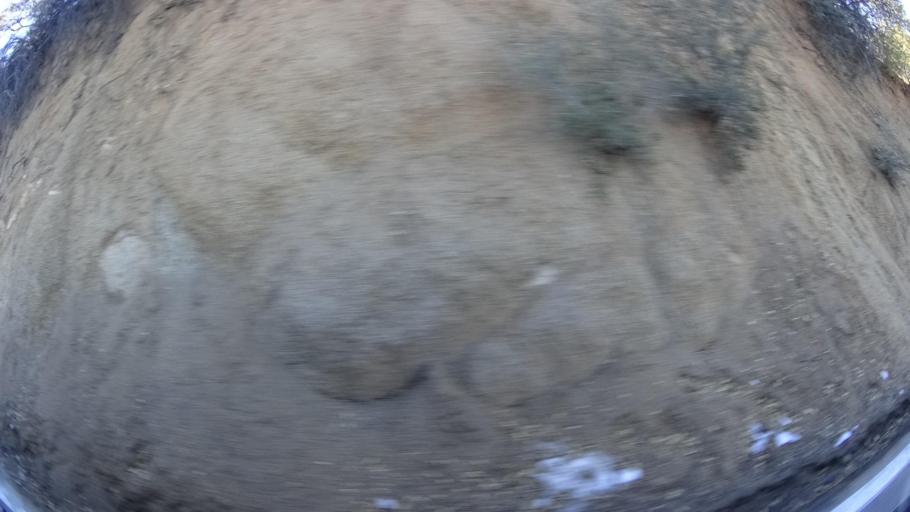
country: US
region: California
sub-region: Kern County
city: Alta Sierra
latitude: 35.7381
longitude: -118.6326
